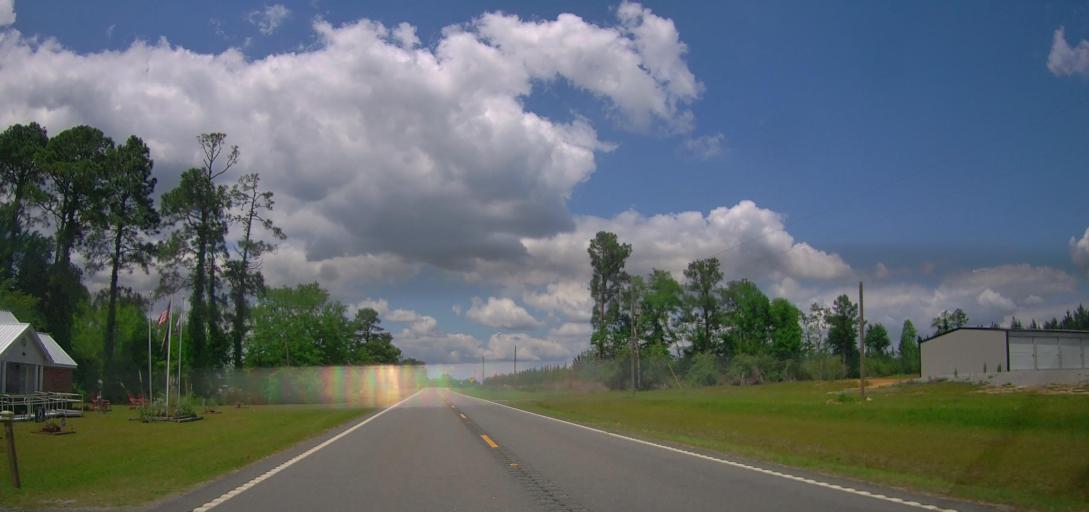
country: US
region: Georgia
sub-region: Treutlen County
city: Soperton
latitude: 32.3992
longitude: -82.6038
